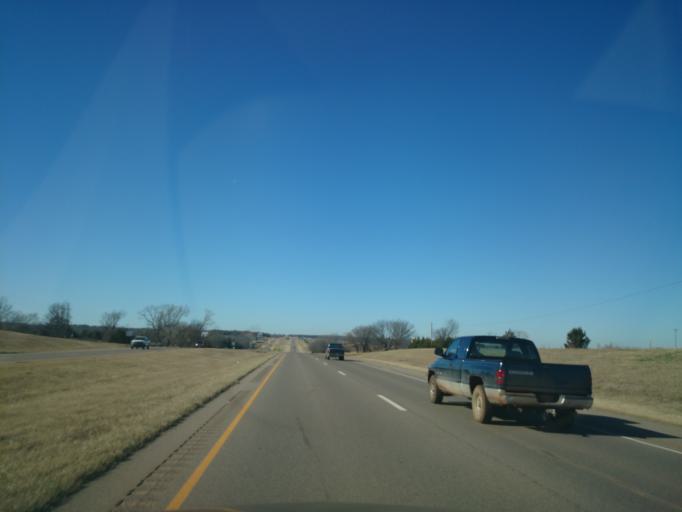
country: US
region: Oklahoma
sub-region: Payne County
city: Stillwater
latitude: 36.1161
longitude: -97.1475
